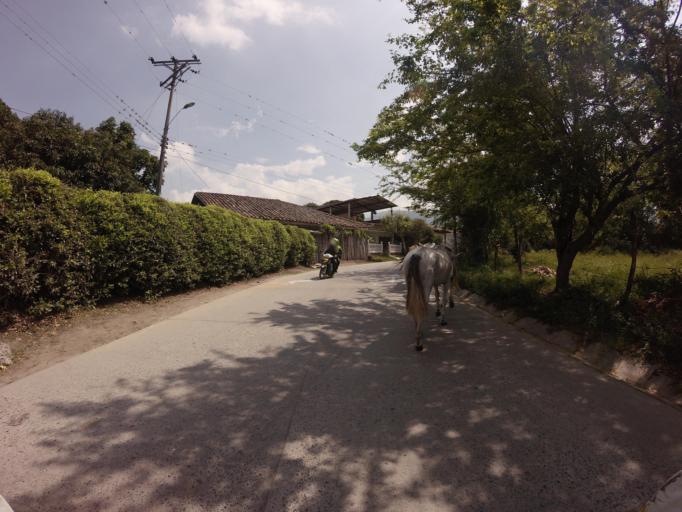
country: CO
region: Valle del Cauca
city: Florida
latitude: 3.3195
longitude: -76.2249
